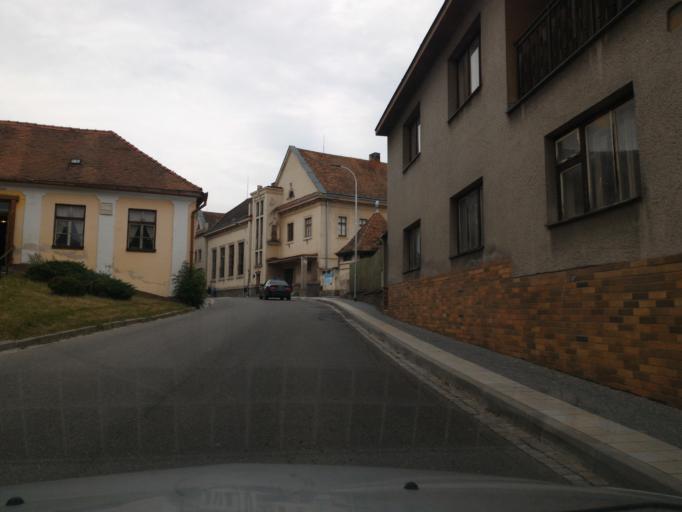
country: CZ
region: Vysocina
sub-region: Okres Jihlava
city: Telc
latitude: 49.1873
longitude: 15.4519
